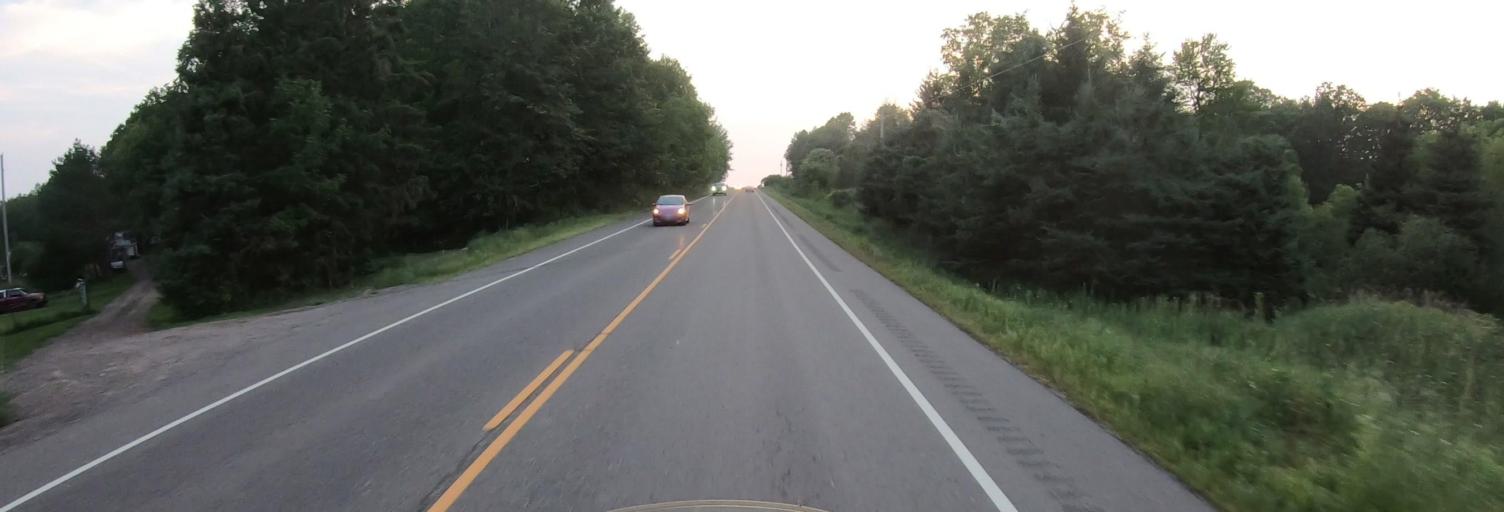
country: US
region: Minnesota
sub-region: Pine County
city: Rock Creek
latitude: 45.7735
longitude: -92.8457
